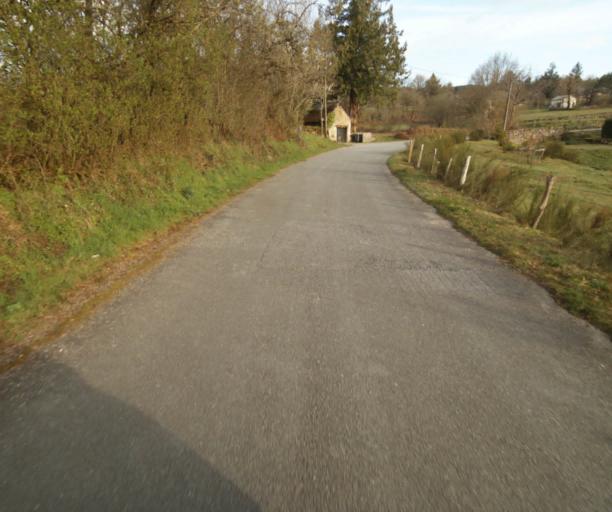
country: FR
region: Limousin
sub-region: Departement de la Correze
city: Correze
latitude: 45.4024
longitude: 1.9001
